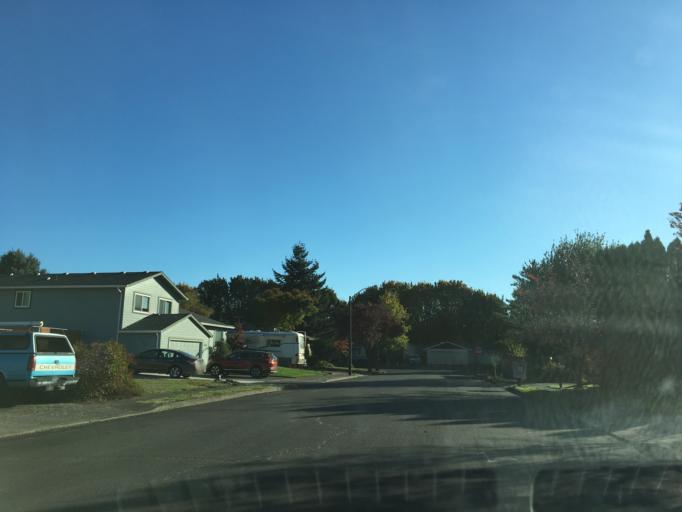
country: US
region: Oregon
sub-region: Multnomah County
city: Wood Village
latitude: 45.5144
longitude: -122.4027
